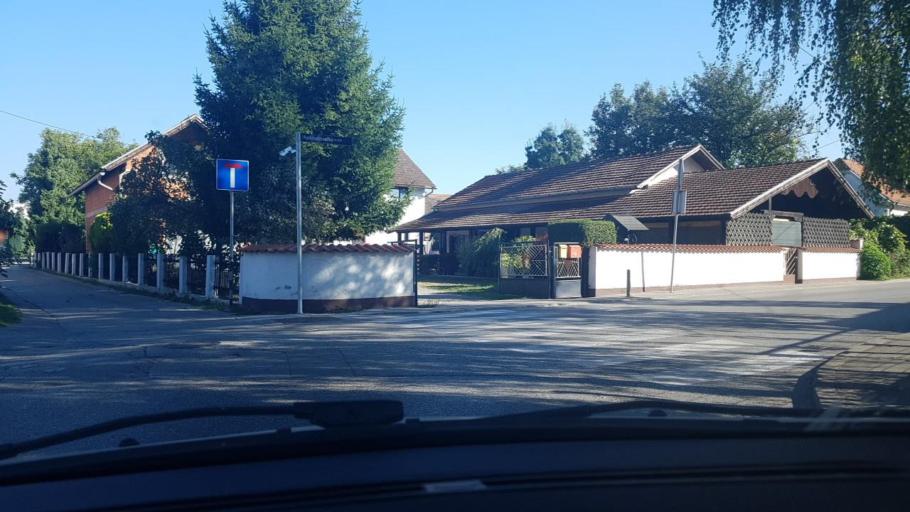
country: HR
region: Grad Zagreb
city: Novi Zagreb
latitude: 45.7681
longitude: 15.9678
